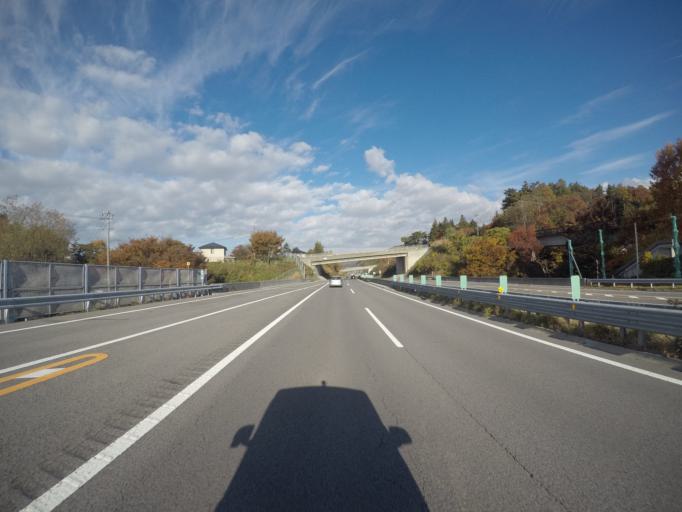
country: JP
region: Nagano
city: Komoro
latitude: 36.3321
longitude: 138.4474
